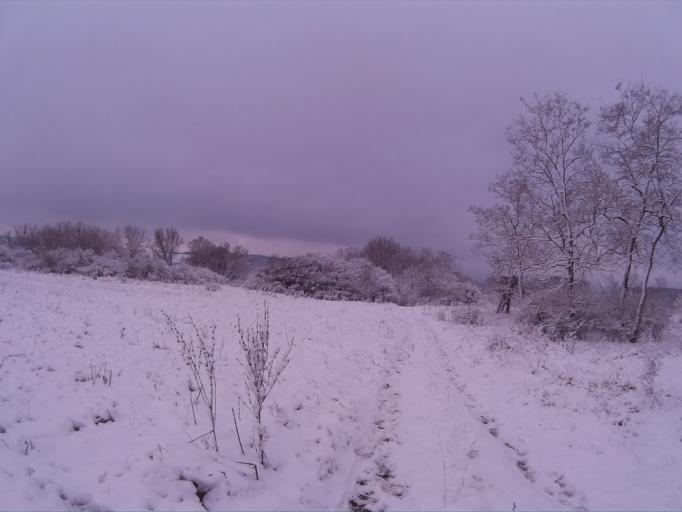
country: HU
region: Fejer
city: Szarliget
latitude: 47.5368
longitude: 18.5386
